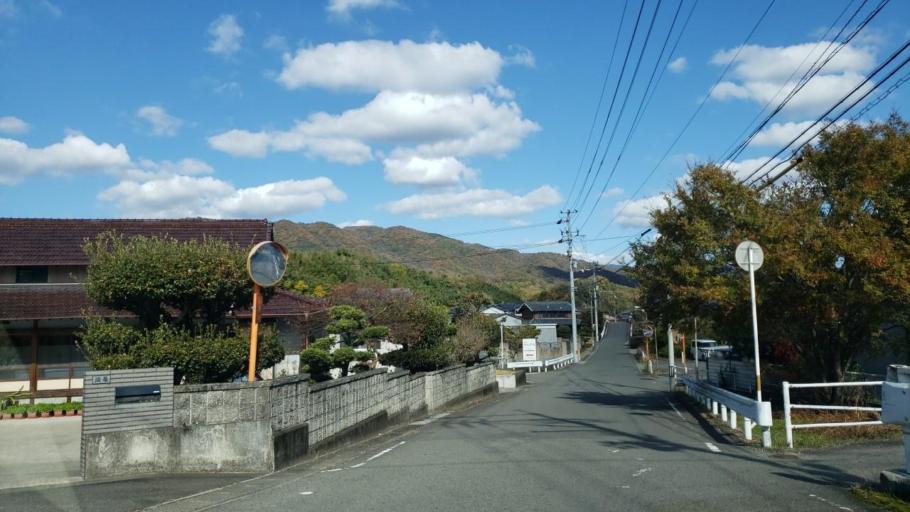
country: JP
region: Tokushima
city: Wakimachi
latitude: 34.0762
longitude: 134.1942
